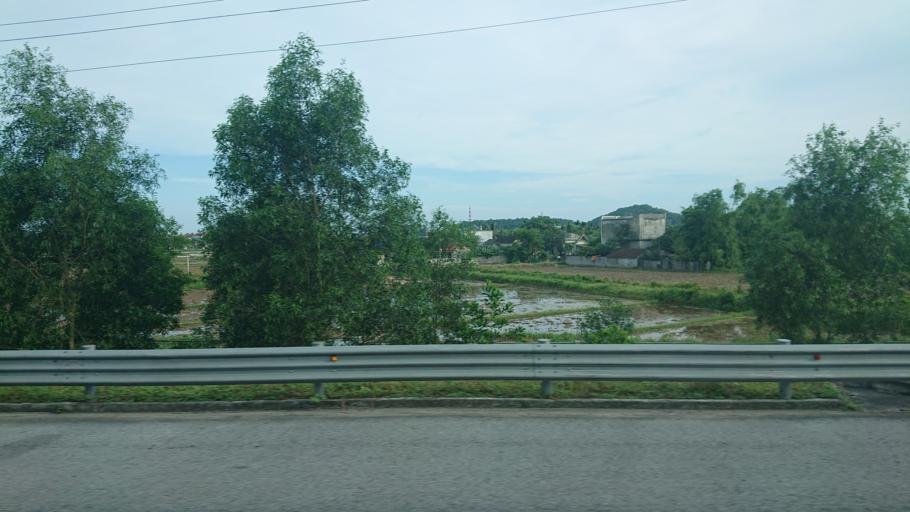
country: VN
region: Hai Phong
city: Nui Doi
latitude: 20.7654
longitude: 106.6694
